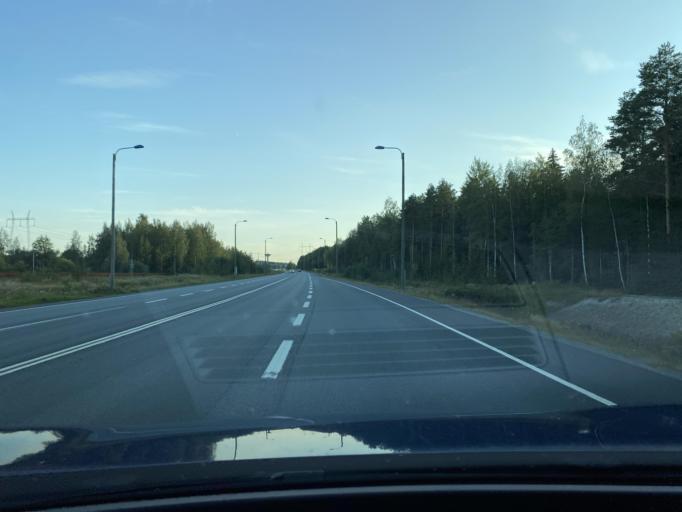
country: FI
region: Southern Ostrobothnia
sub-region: Seinaejoki
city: Nurmo
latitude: 62.8191
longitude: 22.9067
